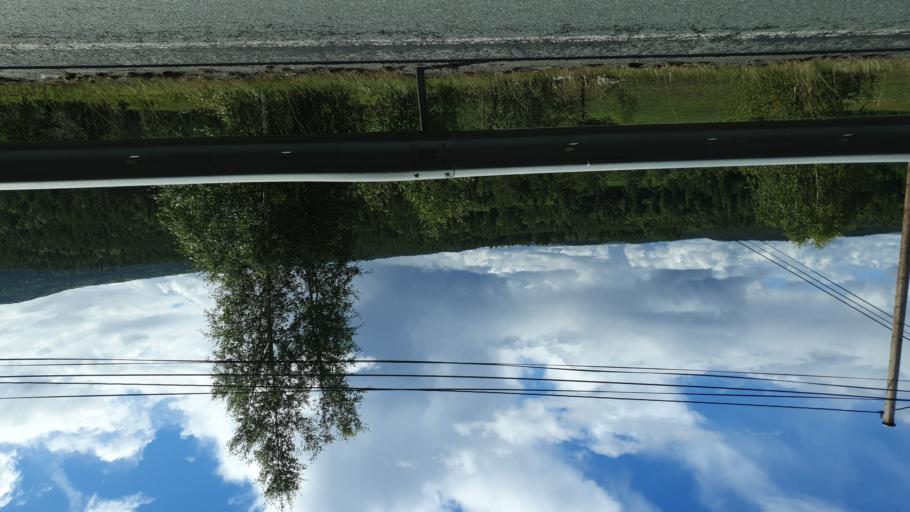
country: NO
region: Sor-Trondelag
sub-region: Rennebu
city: Berkak
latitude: 62.7014
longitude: 9.9488
